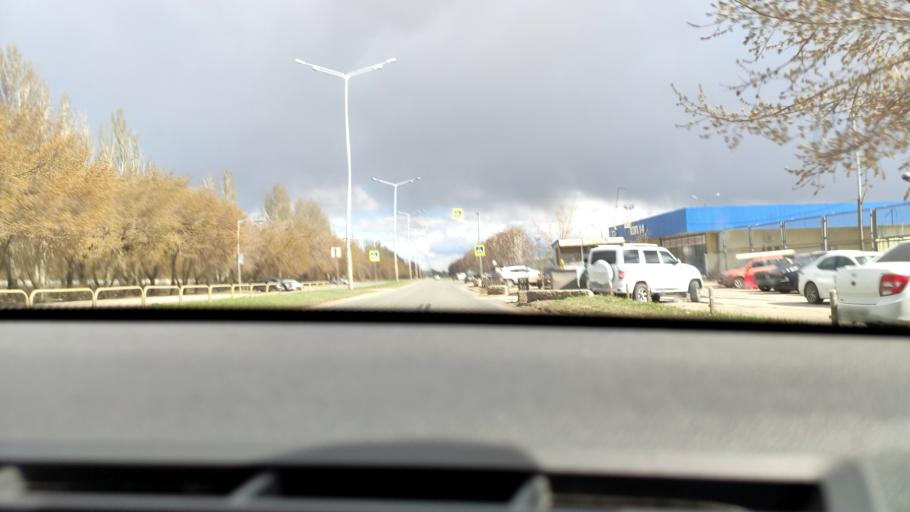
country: RU
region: Samara
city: Tol'yatti
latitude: 53.5689
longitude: 49.2642
